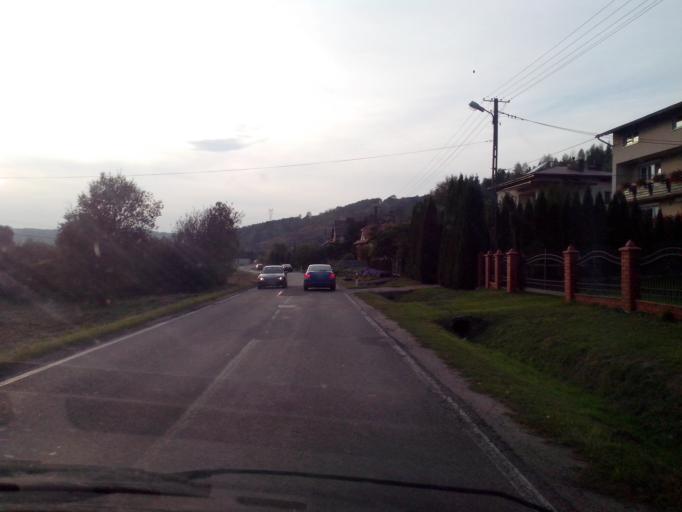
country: PL
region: Subcarpathian Voivodeship
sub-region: Powiat strzyzowski
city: Jawornik
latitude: 49.8086
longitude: 21.8790
